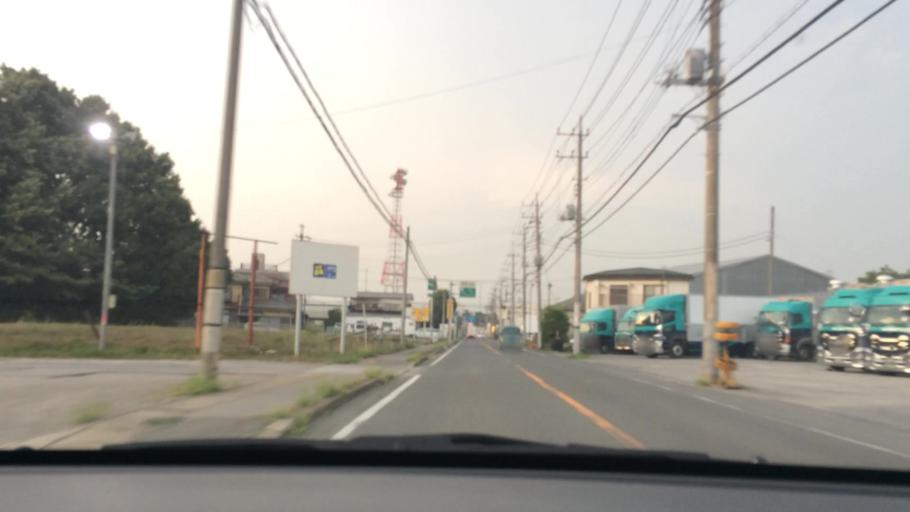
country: JP
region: Chiba
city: Kashiwa
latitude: 35.8842
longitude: 139.9374
